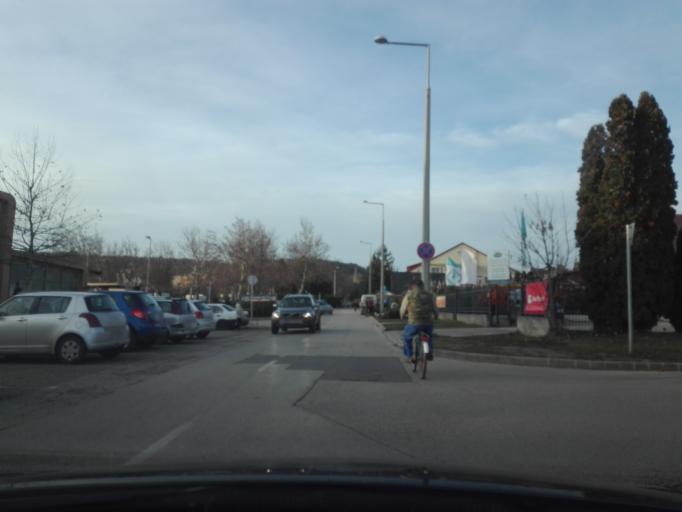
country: HU
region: Veszprem
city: Balatonfured
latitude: 46.9626
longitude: 17.8770
